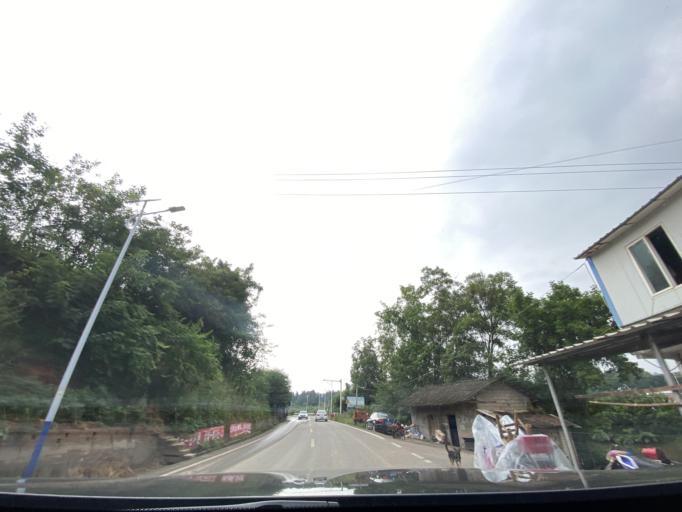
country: CN
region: Sichuan
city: Jiancheng
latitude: 30.5525
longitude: 104.5235
